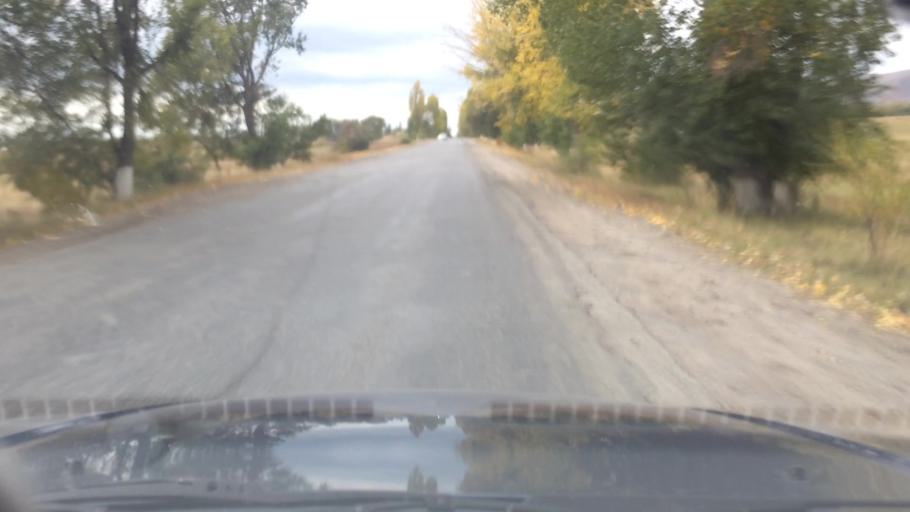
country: KG
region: Ysyk-Koel
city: Tyup
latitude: 42.7745
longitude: 78.2003
